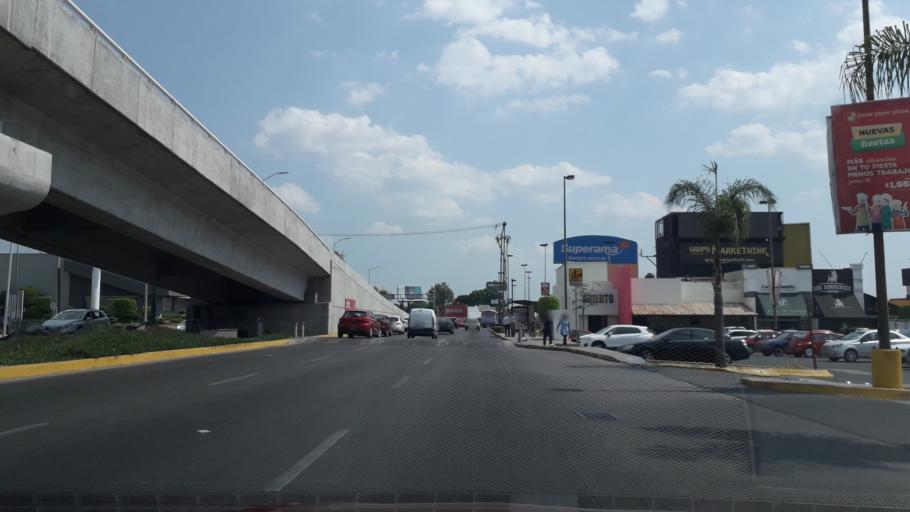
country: MX
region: Puebla
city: Puebla
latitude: 19.0348
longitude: -98.2249
